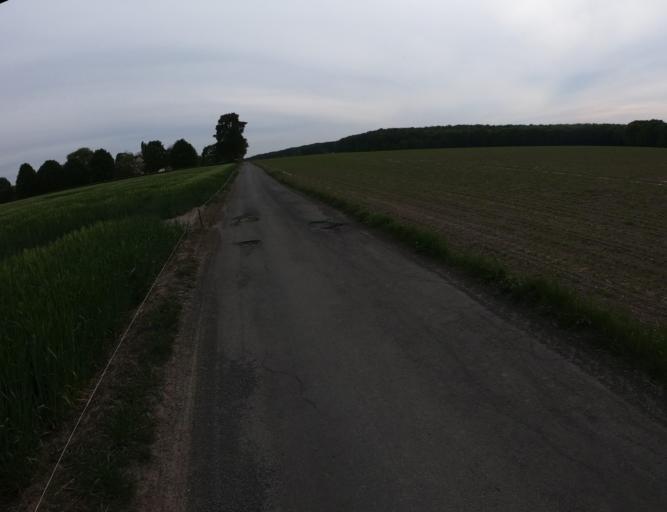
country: BE
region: Wallonia
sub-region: Province du Brabant Wallon
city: Braine-le-Chateau
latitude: 50.7061
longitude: 4.3186
